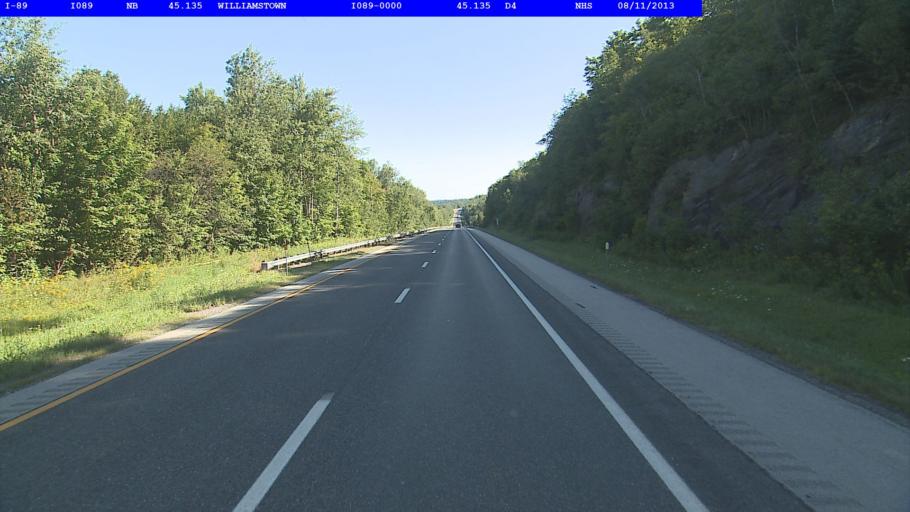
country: US
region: Vermont
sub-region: Orange County
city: Williamstown
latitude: 44.1449
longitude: -72.5940
